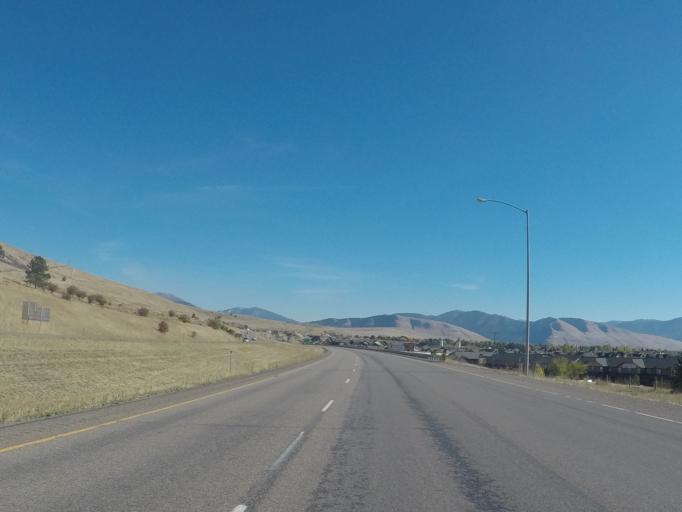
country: US
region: Montana
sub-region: Missoula County
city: Orchard Homes
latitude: 46.9211
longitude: -114.0638
